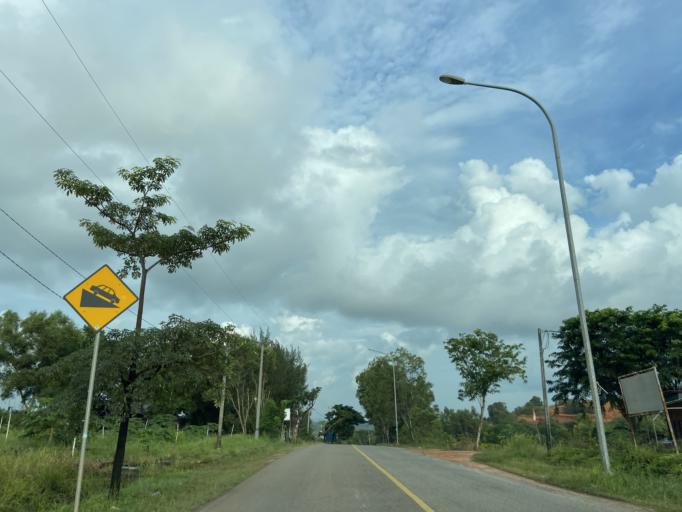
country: ID
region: Riau Islands
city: Tanjungpinang
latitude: 0.9389
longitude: 104.0860
